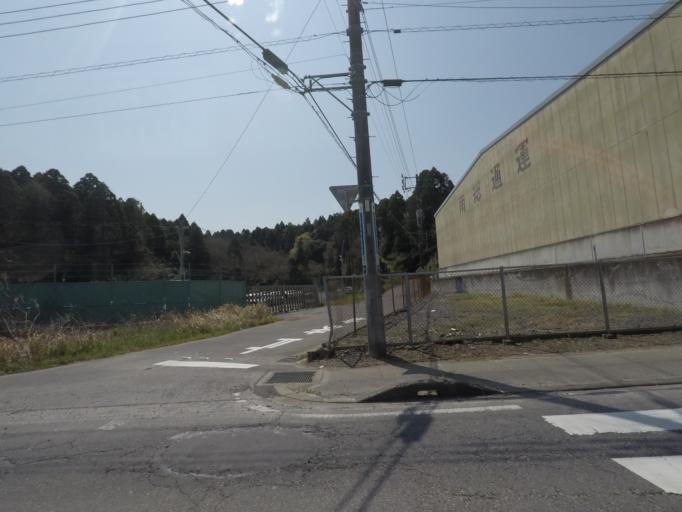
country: JP
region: Chiba
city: Naruto
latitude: 35.6443
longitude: 140.4538
